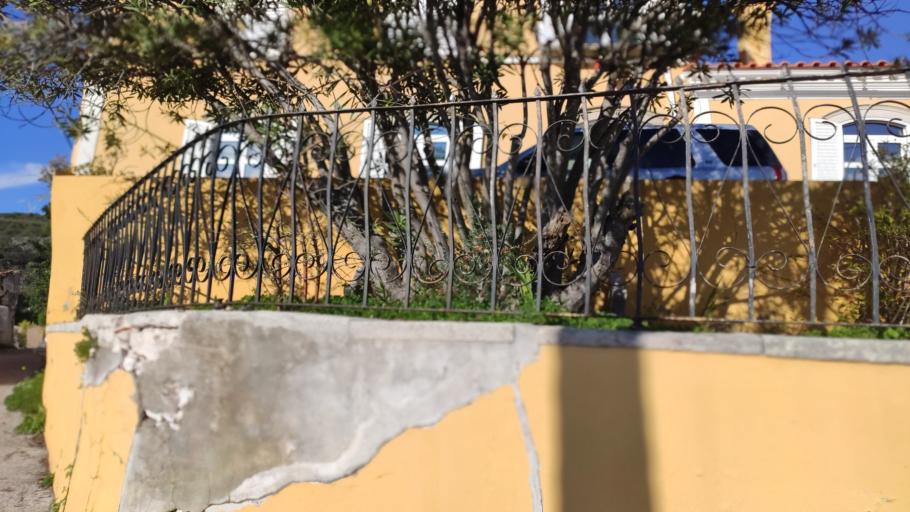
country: PT
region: Faro
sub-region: Sao Bras de Alportel
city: Sao Bras de Alportel
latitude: 37.1541
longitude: -7.9081
